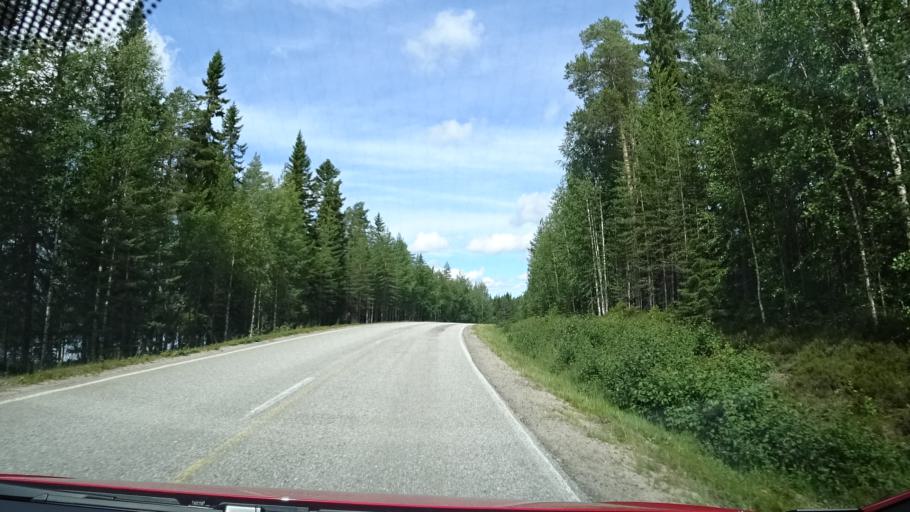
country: FI
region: Kainuu
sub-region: Kehys-Kainuu
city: Kuhmo
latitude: 64.4534
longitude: 29.7746
